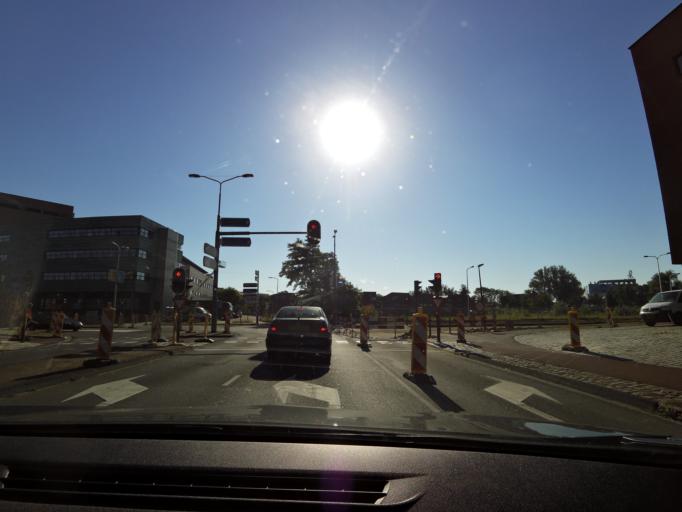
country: NL
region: Overijssel
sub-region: Gemeente Deventer
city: Deventer
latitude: 52.2525
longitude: 6.1677
